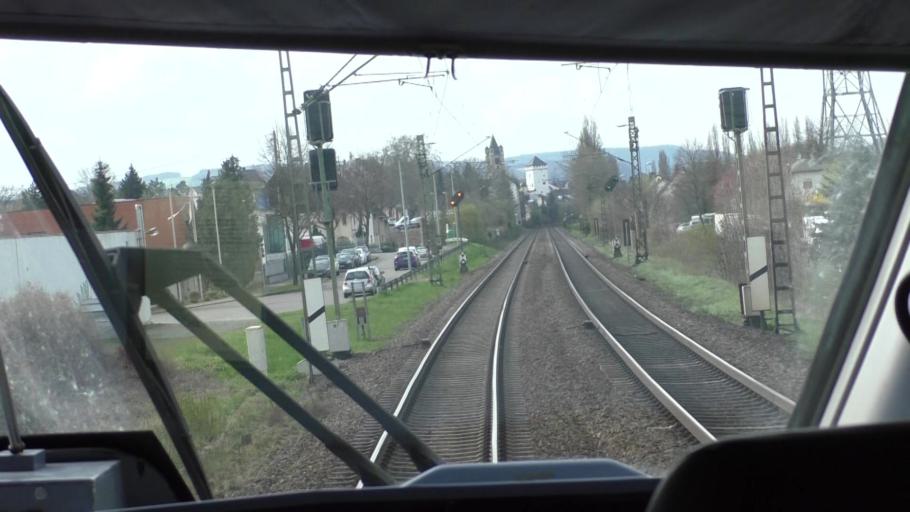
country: DE
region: Rheinland-Pfalz
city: Kettig
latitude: 50.4089
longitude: 7.4753
